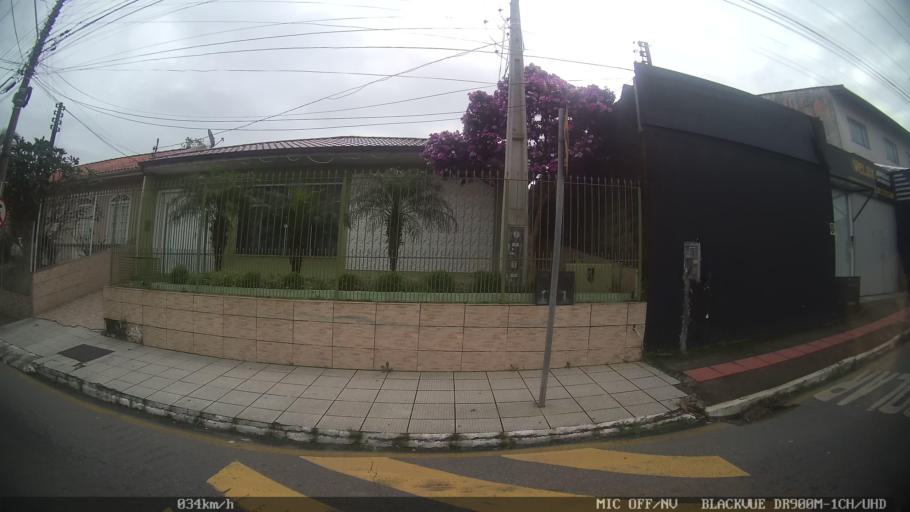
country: BR
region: Santa Catarina
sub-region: Sao Jose
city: Campinas
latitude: -27.5655
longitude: -48.6262
